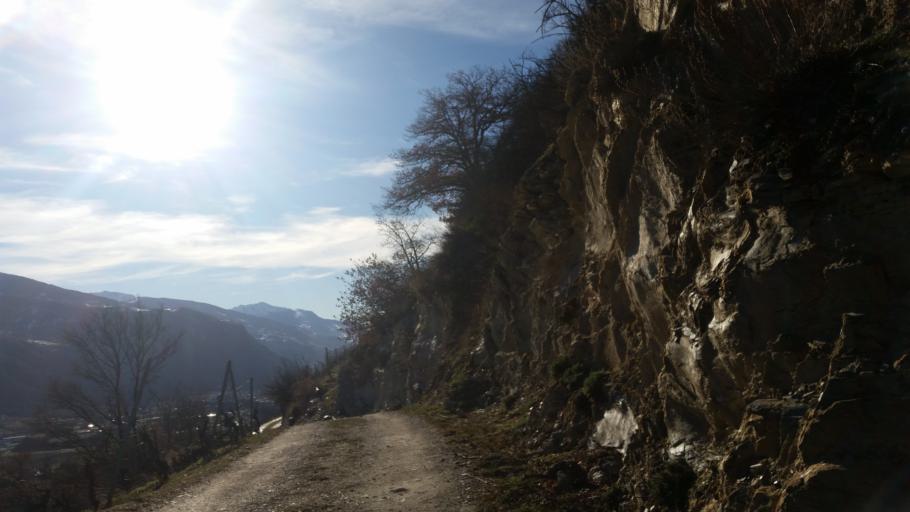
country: CH
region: Valais
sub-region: Sierre District
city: Chalais
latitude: 46.2785
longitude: 7.4937
